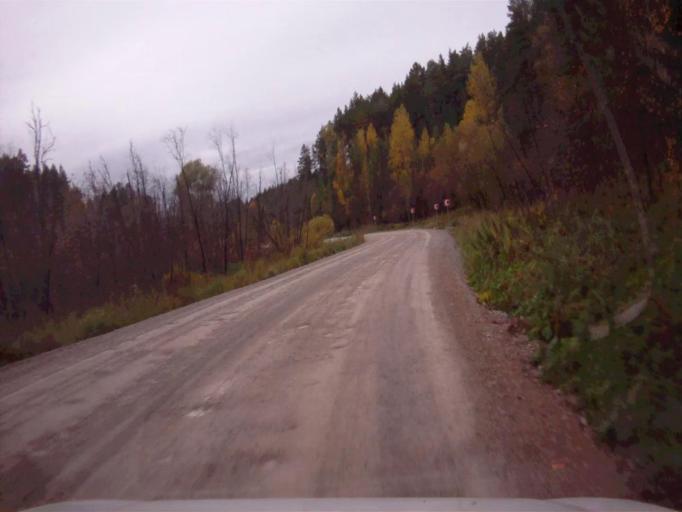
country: RU
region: Chelyabinsk
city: Nyazepetrovsk
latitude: 56.0466
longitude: 59.5030
